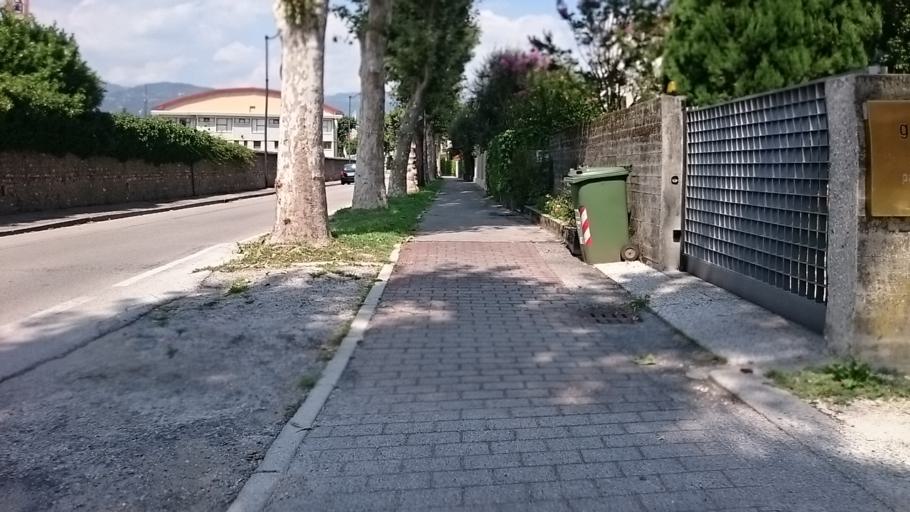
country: IT
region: Veneto
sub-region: Provincia di Vicenza
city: Bassano del Grappa
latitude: 45.7610
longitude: 11.7341
